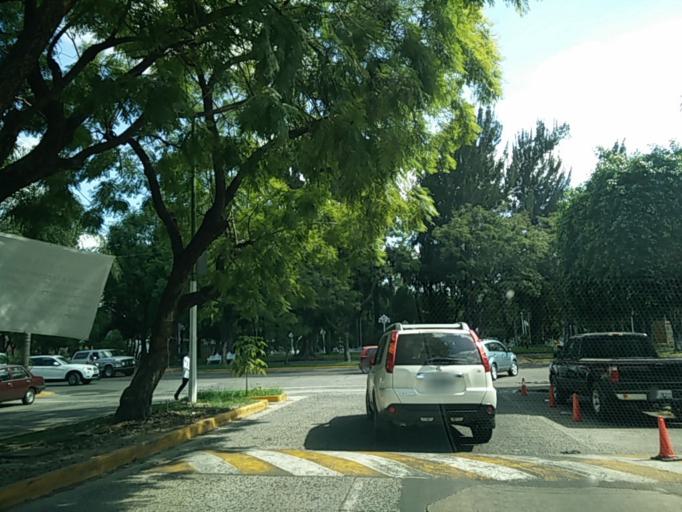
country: MX
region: Jalisco
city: Guadalajara
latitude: 20.6667
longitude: -103.4036
